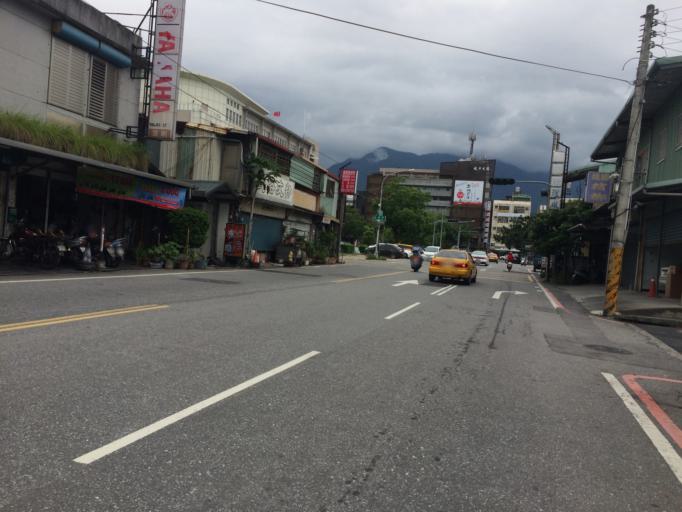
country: TW
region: Taiwan
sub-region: Hualien
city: Hualian
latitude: 23.9838
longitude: 121.6074
